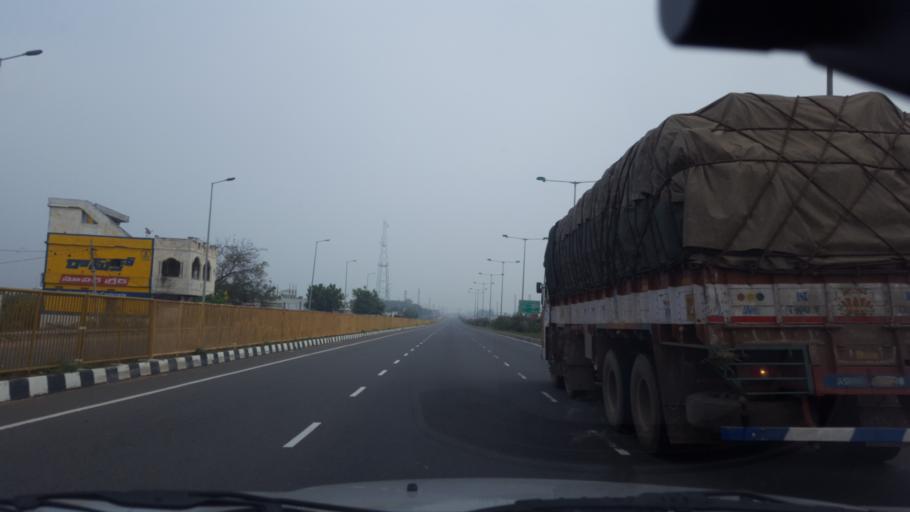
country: IN
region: Andhra Pradesh
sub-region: Prakasam
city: pedda nakkalapalem
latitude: 15.9712
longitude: 80.0961
